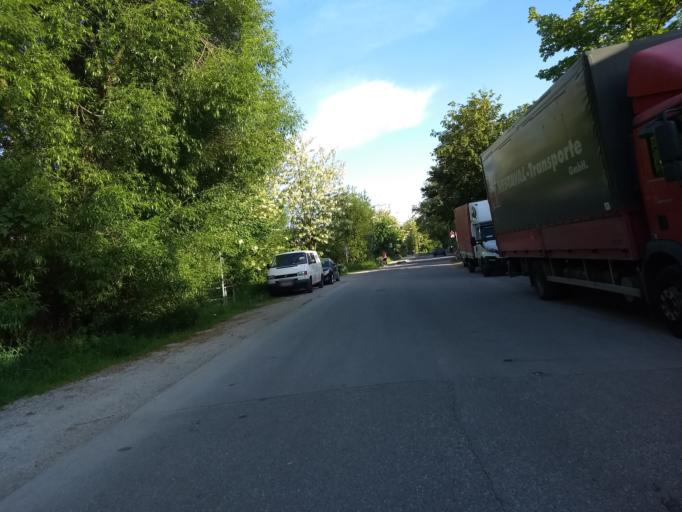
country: AT
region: Salzburg
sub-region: Salzburg Stadt
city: Salzburg
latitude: 47.8216
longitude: 13.0595
